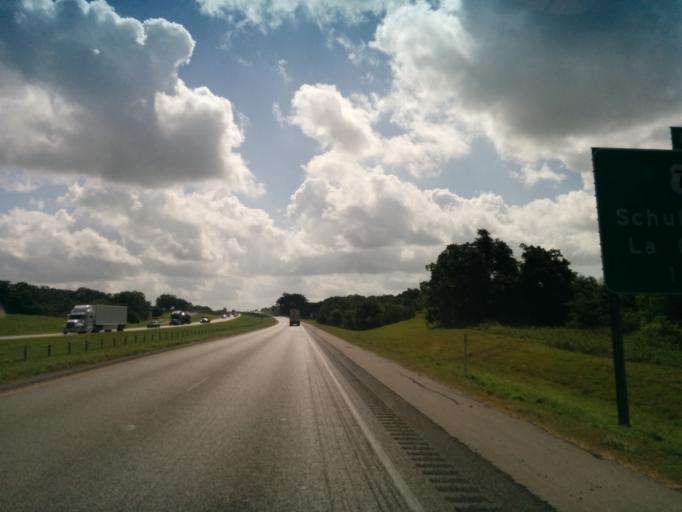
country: US
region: Texas
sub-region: Fayette County
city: Schulenburg
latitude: 29.6905
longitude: -96.9227
